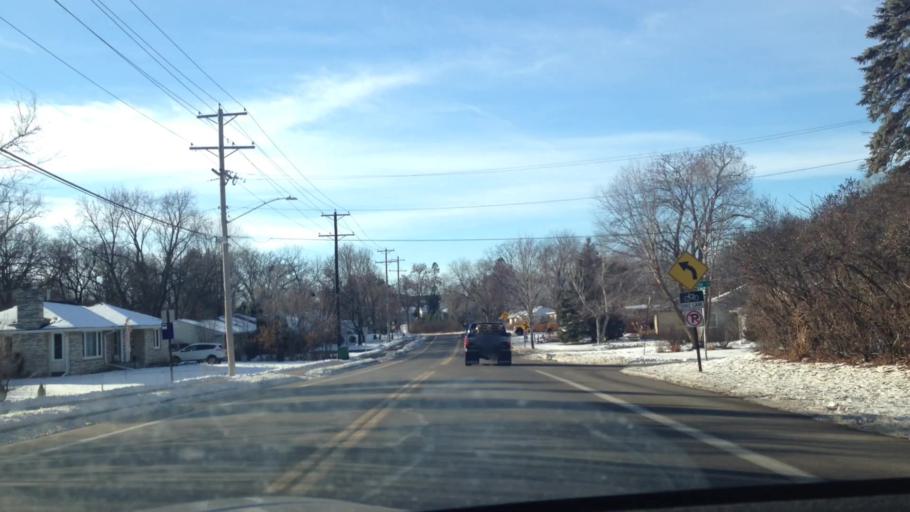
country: US
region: Minnesota
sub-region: Hennepin County
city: Minnetonka Mills
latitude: 44.9486
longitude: -93.3953
